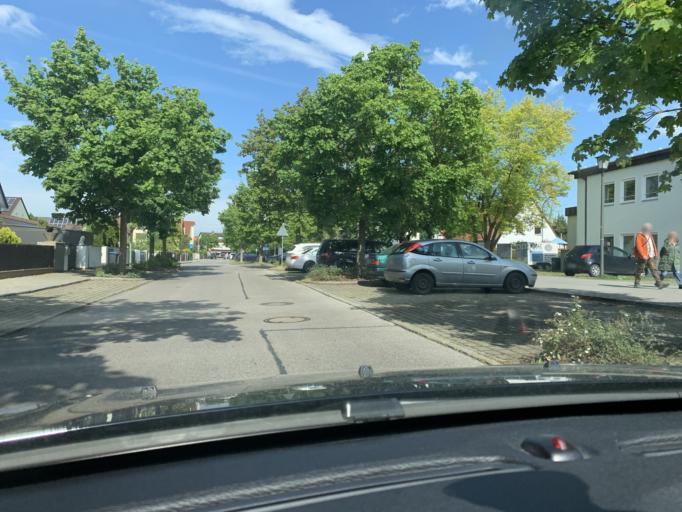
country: DE
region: Bavaria
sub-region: Upper Bavaria
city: Unterschleissheim
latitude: 48.2782
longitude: 11.5809
